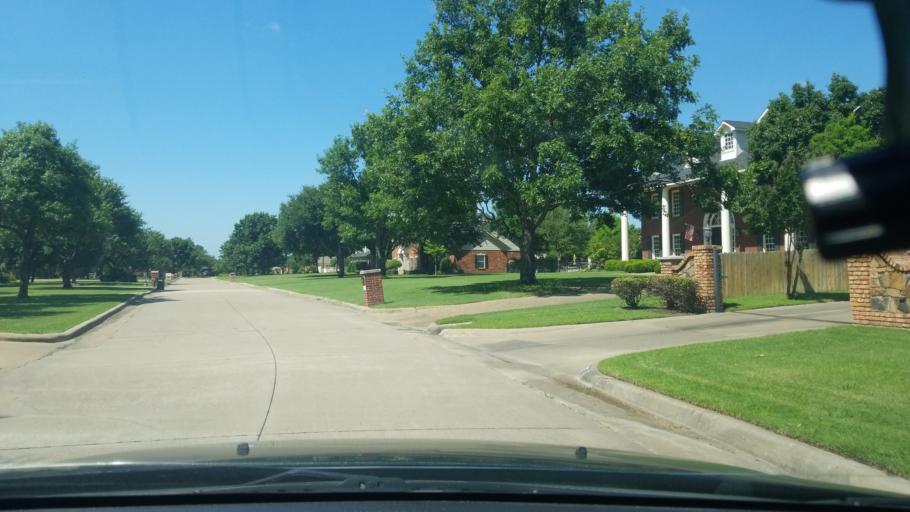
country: US
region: Texas
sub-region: Dallas County
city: Sunnyvale
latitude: 32.8017
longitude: -96.5907
